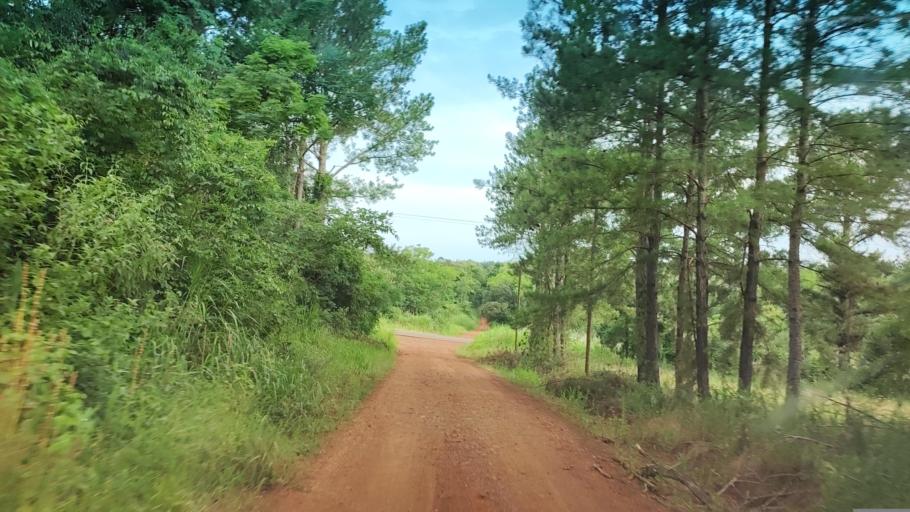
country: AR
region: Misiones
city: Gobernador Roca
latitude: -27.1717
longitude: -55.4492
